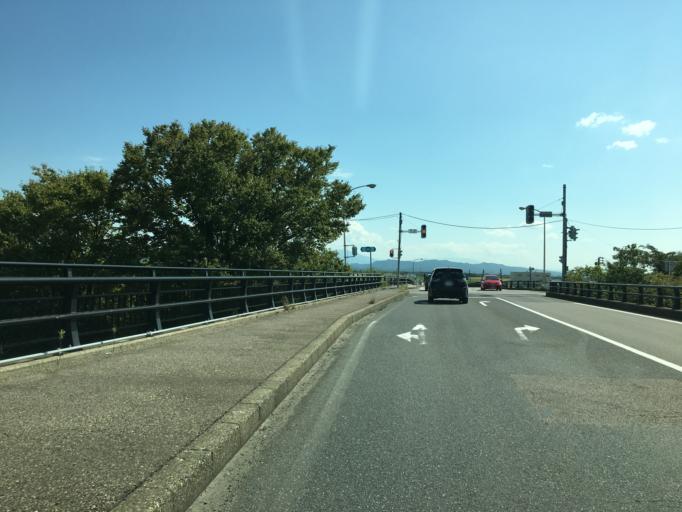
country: JP
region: Niigata
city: Kameda-honcho
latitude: 37.8355
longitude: 139.0964
